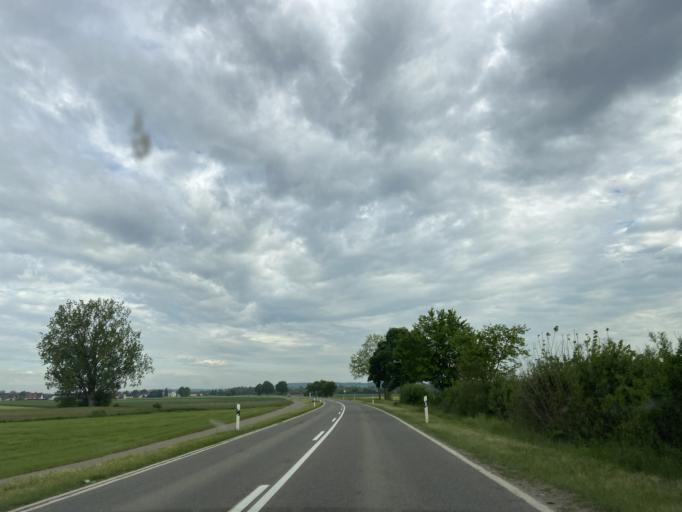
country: DE
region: Baden-Wuerttemberg
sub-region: Tuebingen Region
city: Hohentengen
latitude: 48.0457
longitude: 9.3591
